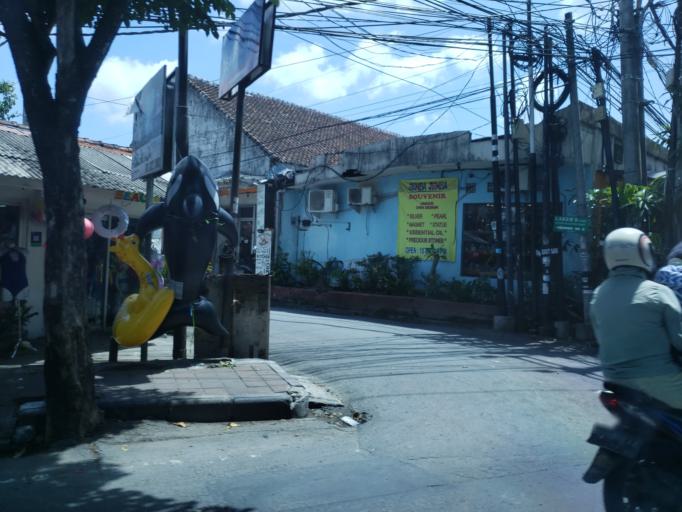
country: ID
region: Bali
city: Jimbaran
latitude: -8.7783
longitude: 115.1691
